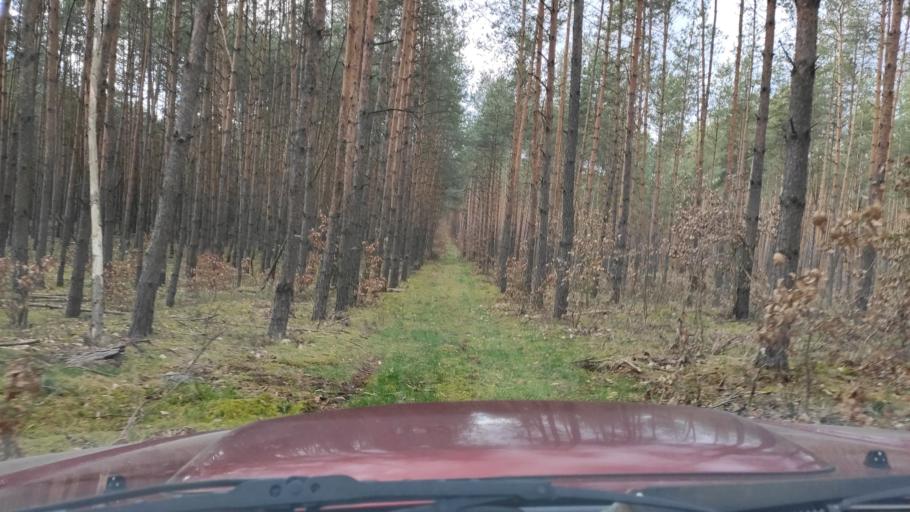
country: PL
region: Masovian Voivodeship
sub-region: Powiat kozienicki
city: Garbatka-Letnisko
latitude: 51.5128
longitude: 21.5704
